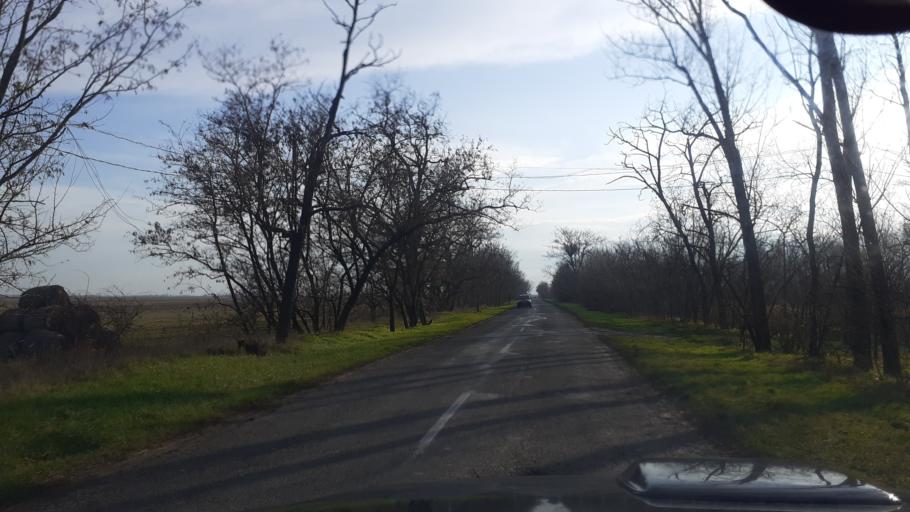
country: HU
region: Bacs-Kiskun
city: Kunszentmiklos
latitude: 47.0952
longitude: 19.0930
